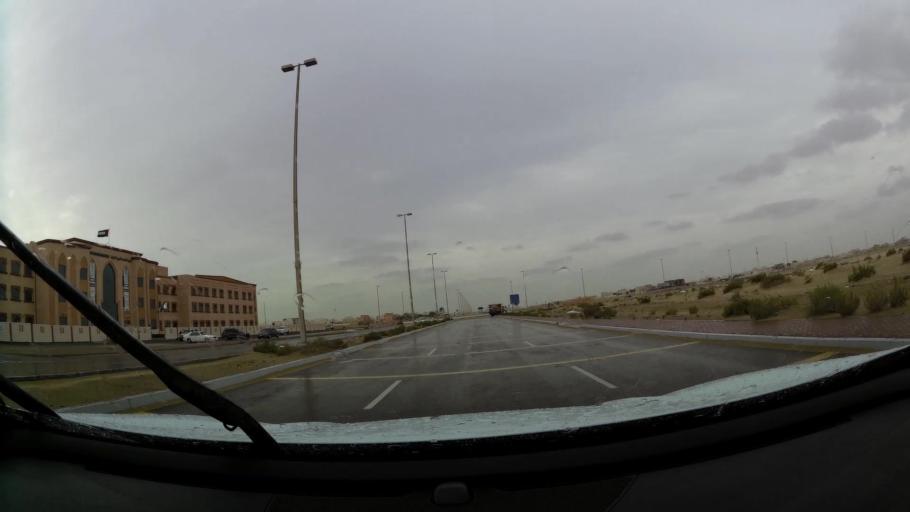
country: AE
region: Abu Dhabi
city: Abu Dhabi
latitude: 24.3615
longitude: 54.6343
